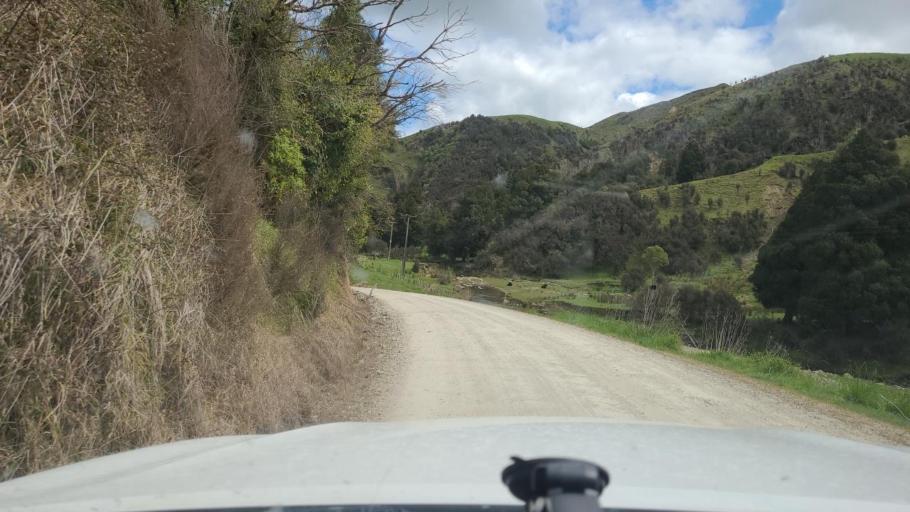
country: NZ
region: Gisborne
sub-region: Gisborne District
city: Gisborne
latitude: -38.8290
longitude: 177.7251
